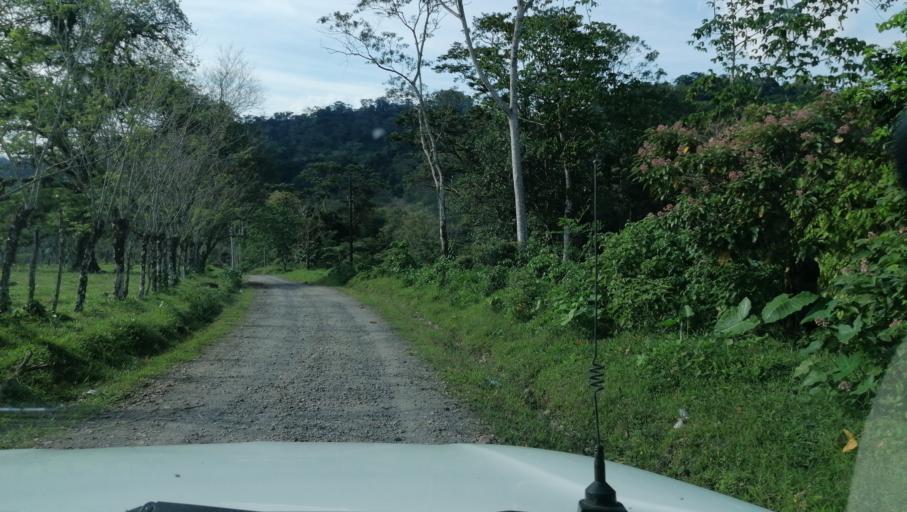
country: MX
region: Chiapas
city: Ostuacan
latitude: 17.4716
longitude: -93.2365
